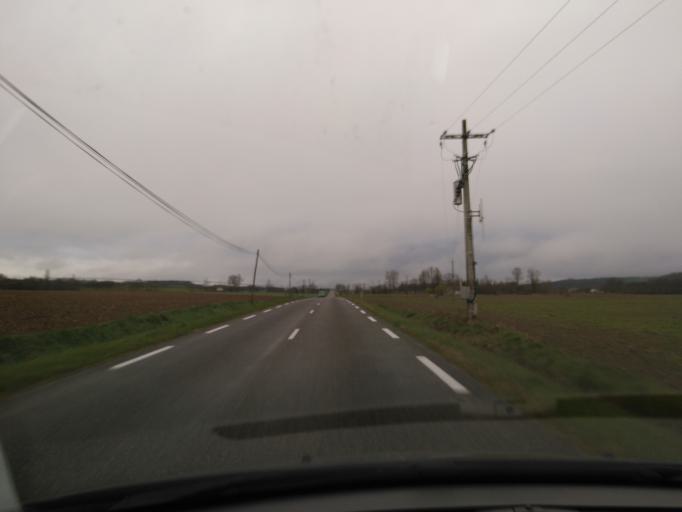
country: FR
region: Midi-Pyrenees
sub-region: Departement de la Haute-Garonne
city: Montesquieu-Volvestre
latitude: 43.1700
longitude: 1.2637
